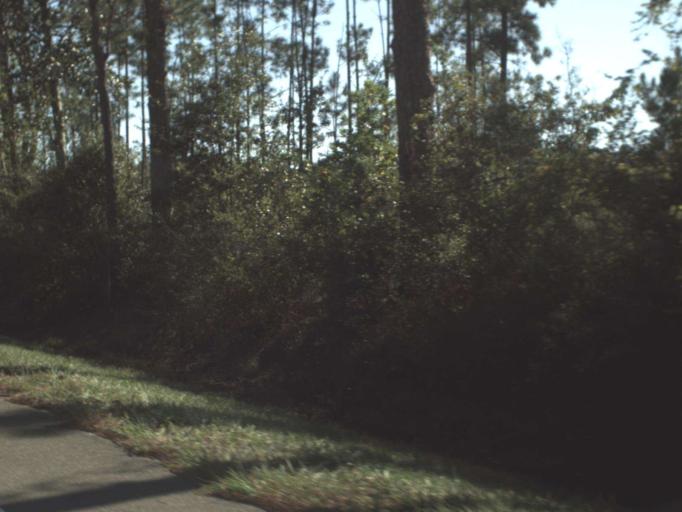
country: US
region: Florida
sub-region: Walton County
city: Freeport
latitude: 30.4838
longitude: -85.9521
